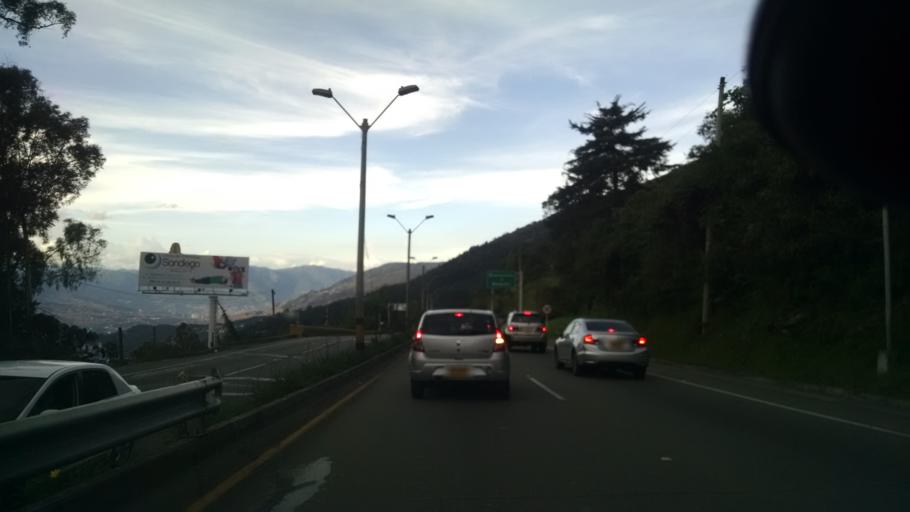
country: CO
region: Antioquia
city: Envigado
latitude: 6.1738
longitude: -75.5465
